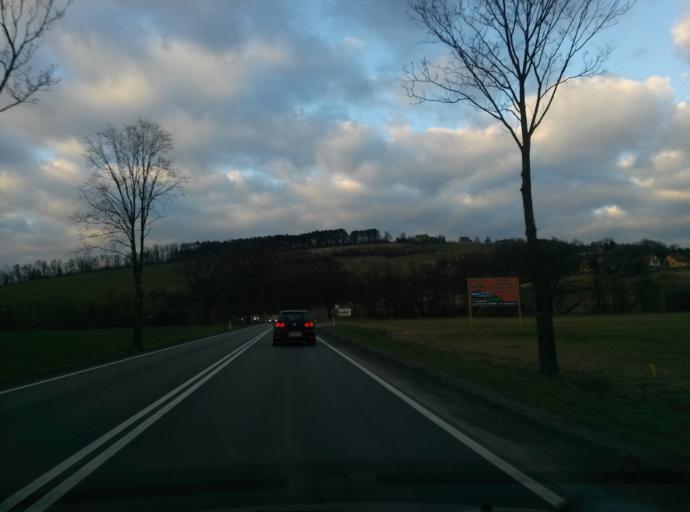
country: PL
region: Lesser Poland Voivodeship
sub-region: Powiat brzeski
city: Okocim
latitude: 49.9402
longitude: 20.5894
